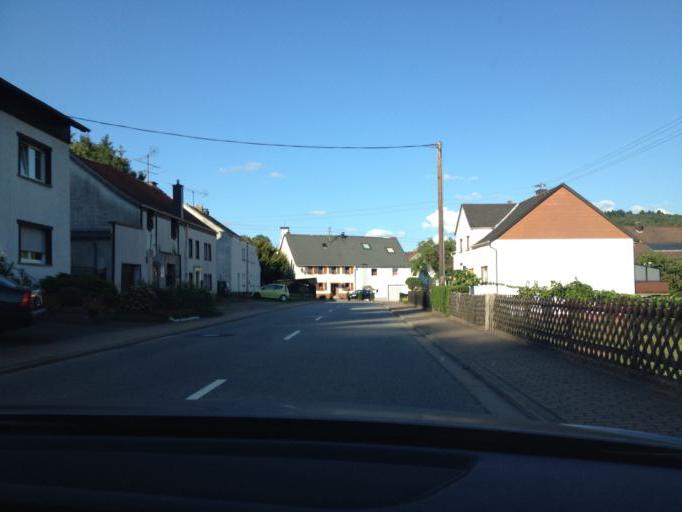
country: DE
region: Saarland
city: Wadern
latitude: 49.4918
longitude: 6.8617
